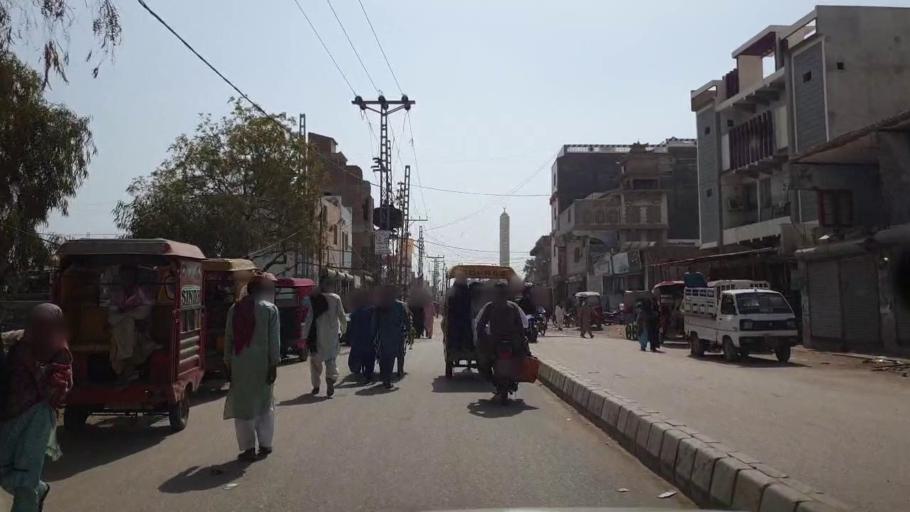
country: PK
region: Sindh
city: Matli
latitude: 25.0443
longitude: 68.6571
